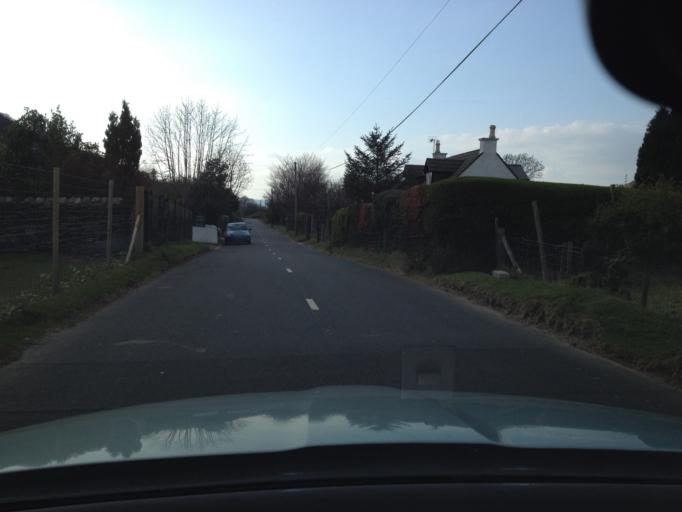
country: GB
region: Scotland
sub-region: North Ayrshire
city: Isle of Arran
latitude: 55.7002
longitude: -5.2801
